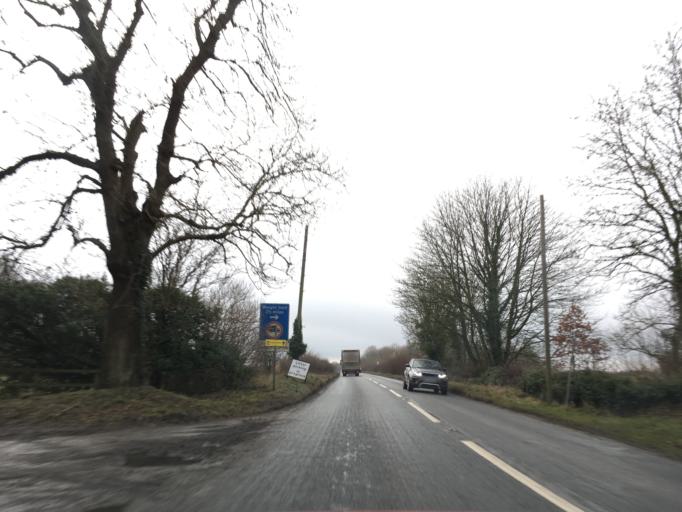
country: GB
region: England
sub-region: Gloucestershire
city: Tetbury
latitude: 51.6573
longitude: -2.1258
